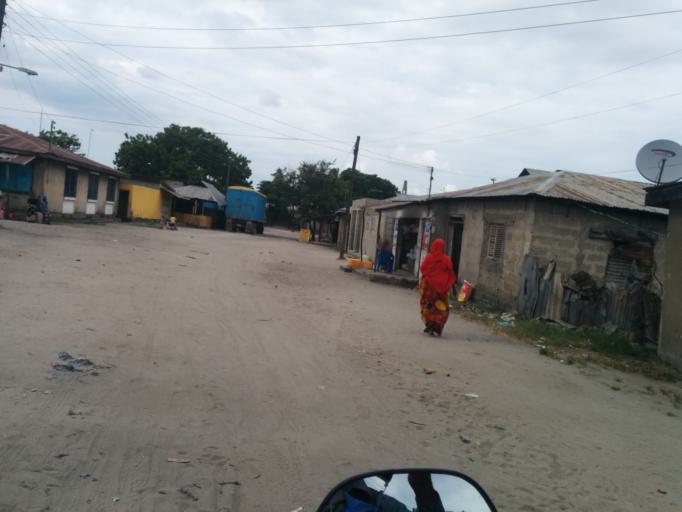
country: TZ
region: Dar es Salaam
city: Dar es Salaam
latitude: -6.8638
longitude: 39.2530
